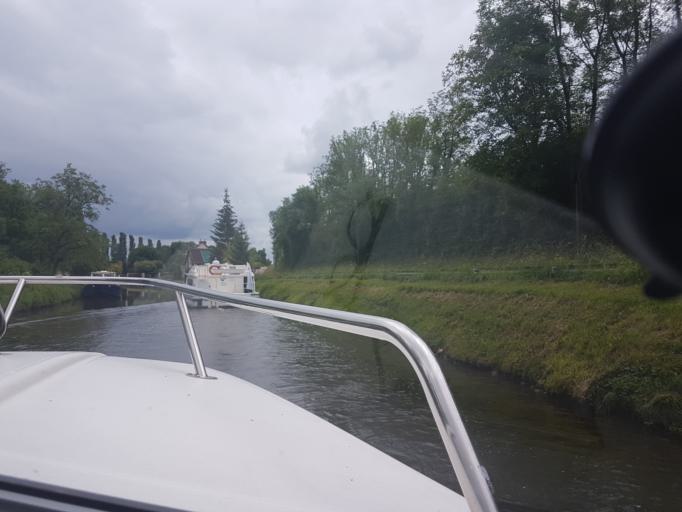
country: FR
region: Bourgogne
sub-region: Departement de l'Yonne
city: Champs-sur-Yonne
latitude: 47.7393
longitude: 3.5907
